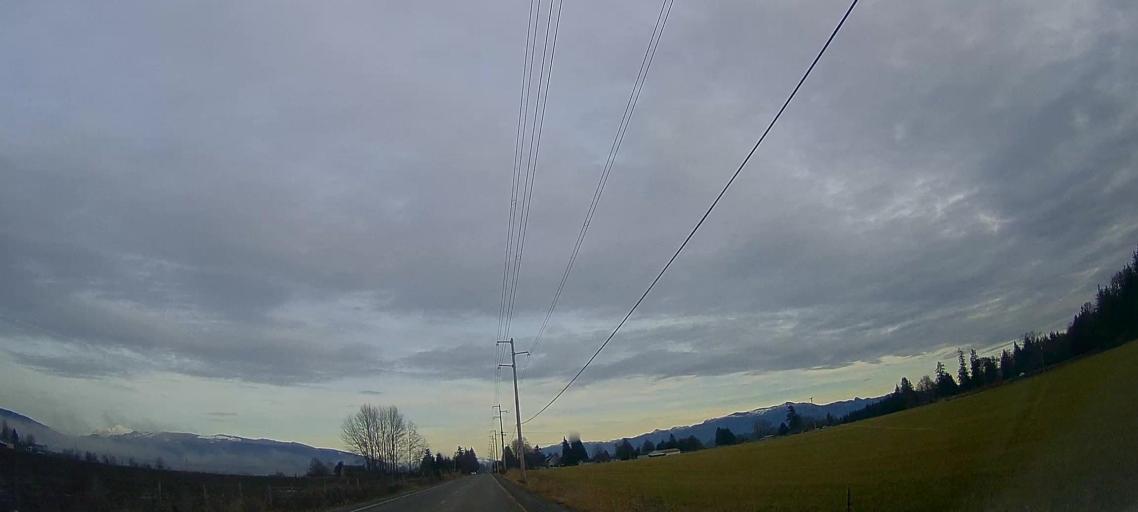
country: US
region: Washington
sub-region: Skagit County
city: Burlington
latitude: 48.5167
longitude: -122.4384
